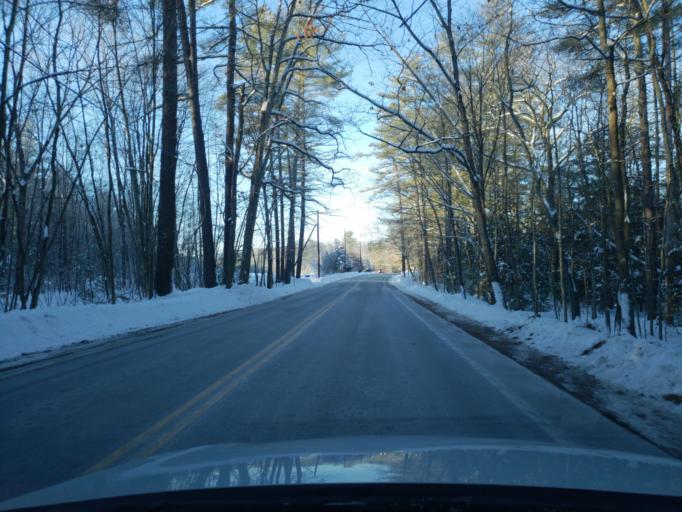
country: US
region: New Hampshire
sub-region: Hillsborough County
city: Goffstown
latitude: 43.0154
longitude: -71.6395
